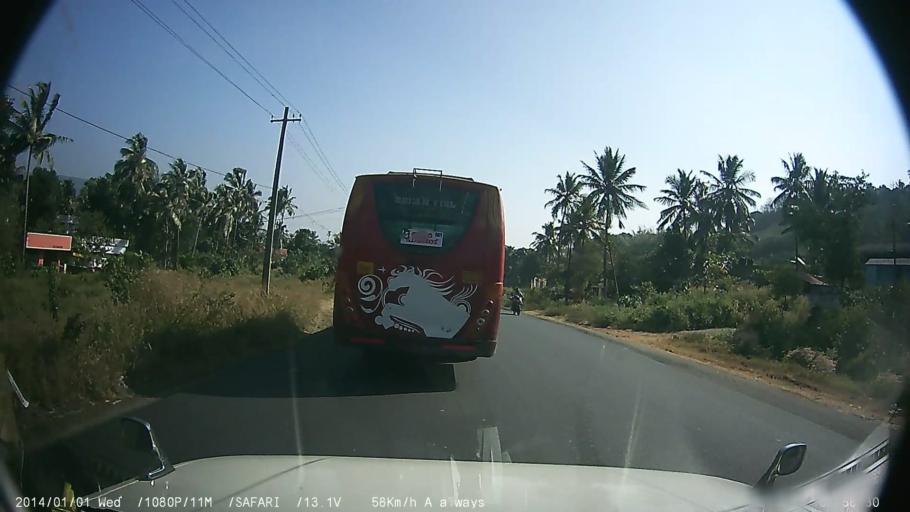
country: IN
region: Kerala
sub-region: Thrissur District
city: Trichur
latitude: 10.5473
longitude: 76.3014
